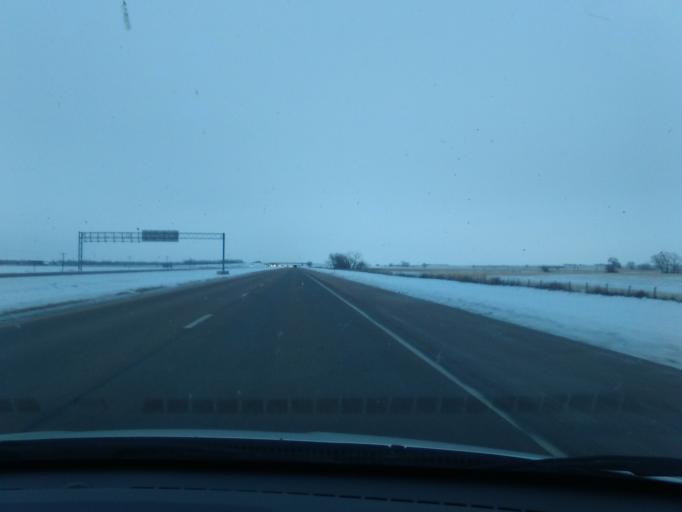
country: US
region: Nebraska
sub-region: Keith County
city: Ogallala
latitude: 41.1204
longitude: -101.6686
